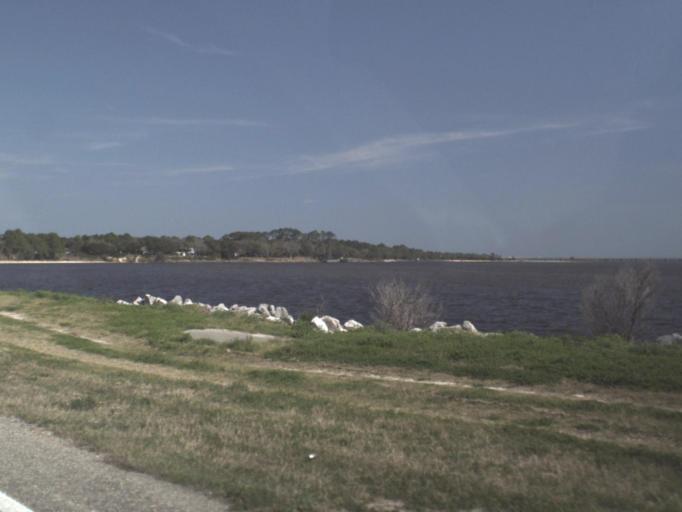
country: US
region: Florida
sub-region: Franklin County
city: Eastpoint
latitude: 29.7346
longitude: -84.9071
